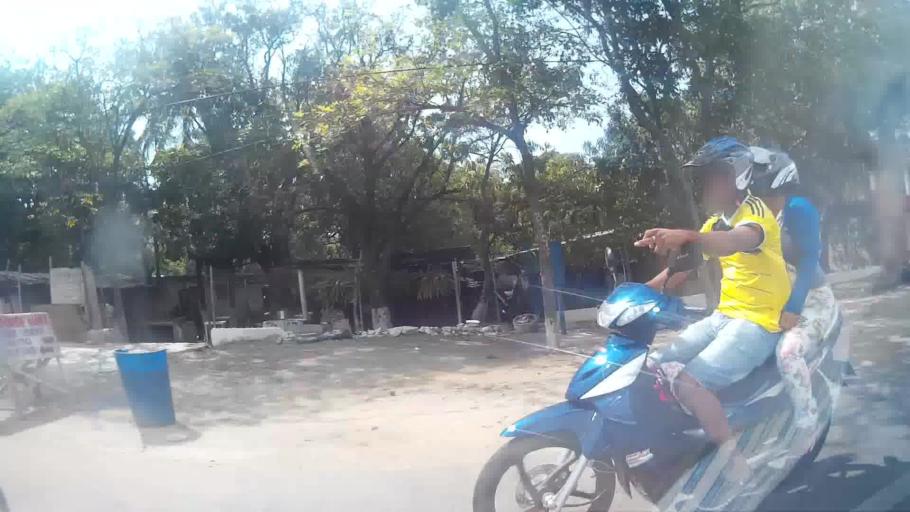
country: CO
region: Magdalena
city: Santa Marta
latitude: 11.1889
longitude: -74.2152
